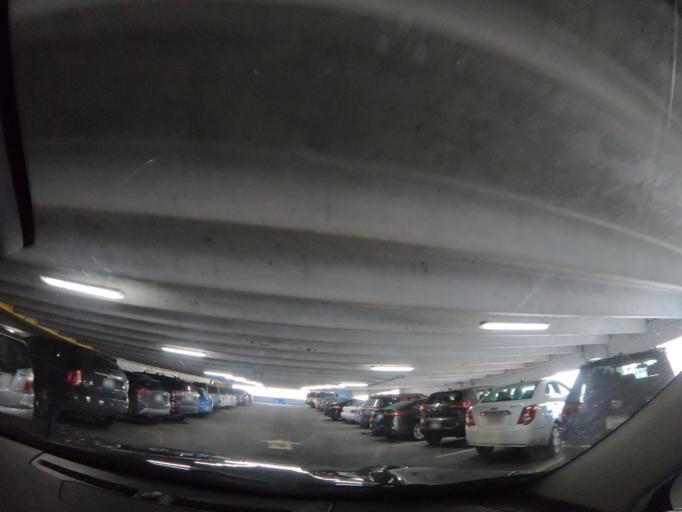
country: US
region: Kentucky
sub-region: Jefferson County
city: Louisville
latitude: 38.2507
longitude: -85.7582
